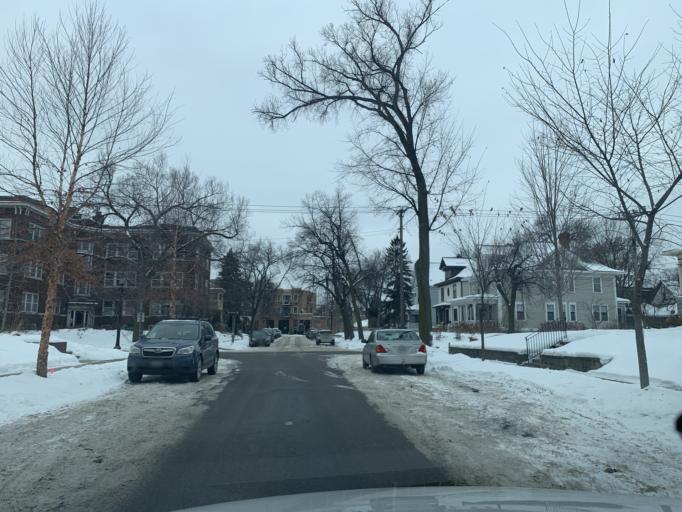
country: US
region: Minnesota
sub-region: Hennepin County
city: Minneapolis
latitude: 44.9577
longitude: -93.2970
